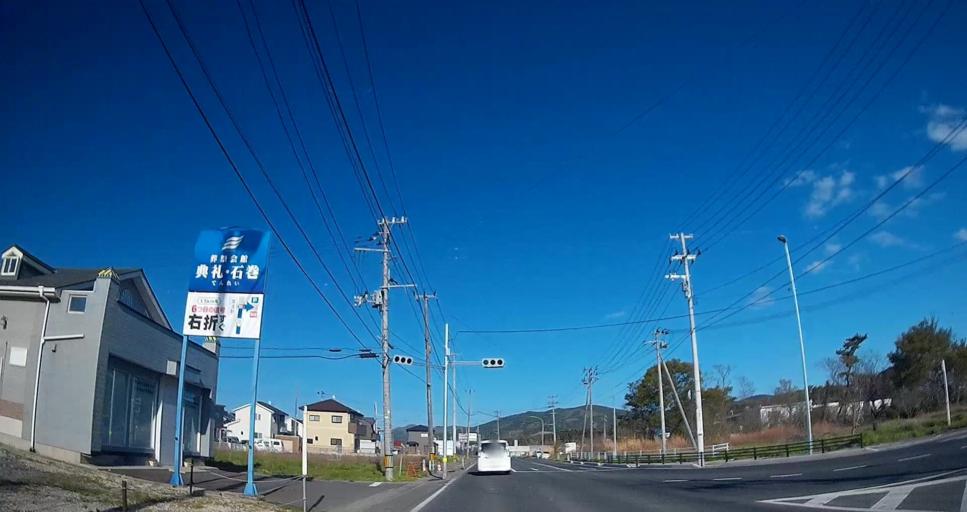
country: JP
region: Miyagi
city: Ishinomaki
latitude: 38.4174
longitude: 141.3456
